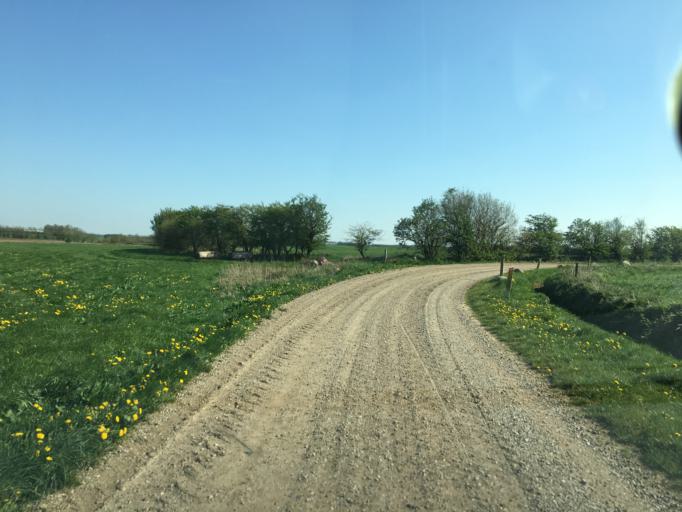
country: DK
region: South Denmark
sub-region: Tonder Kommune
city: Toftlund
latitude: 55.1653
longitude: 9.0977
